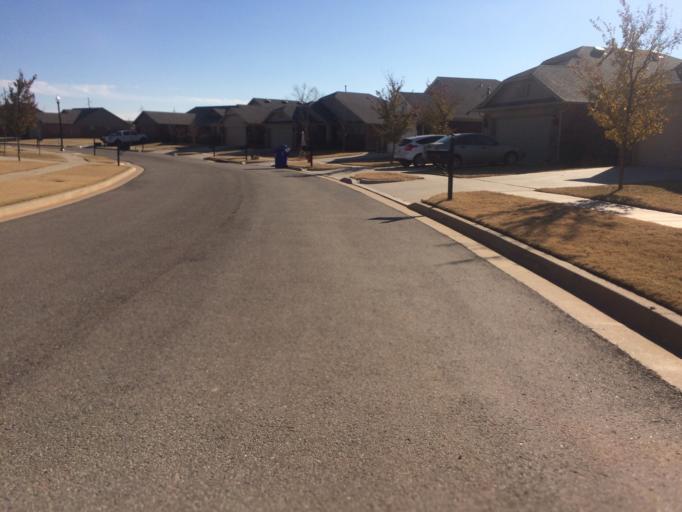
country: US
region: Oklahoma
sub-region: Cleveland County
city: Norman
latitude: 35.2525
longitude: -97.4567
